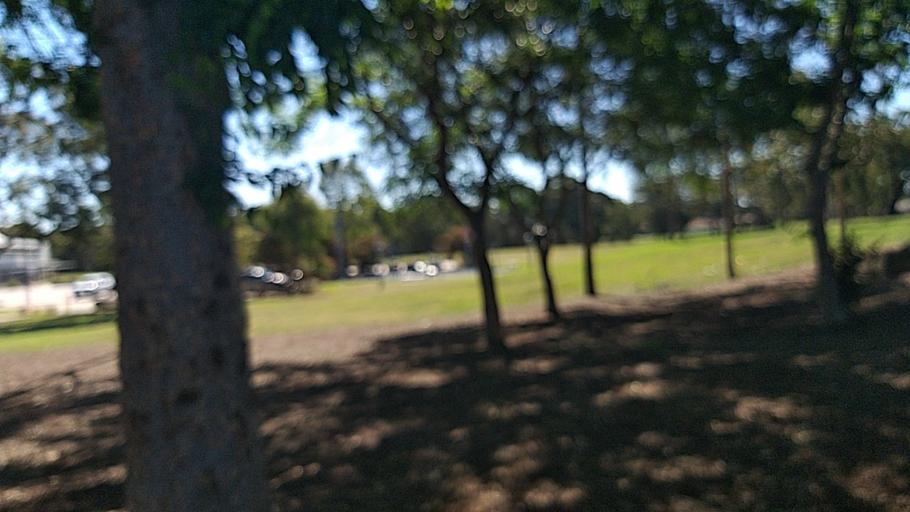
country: AU
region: New South Wales
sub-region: Liverpool
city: Miller
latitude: -33.9265
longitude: 150.9142
